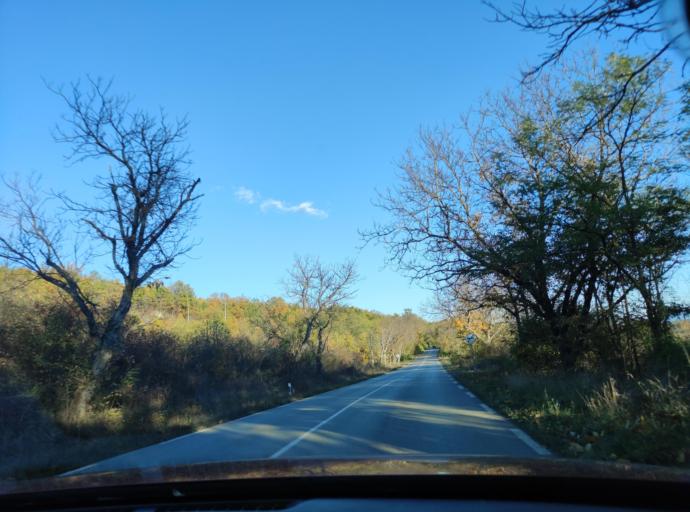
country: BG
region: Montana
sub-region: Obshtina Montana
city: Montana
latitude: 43.4049
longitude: 23.0723
